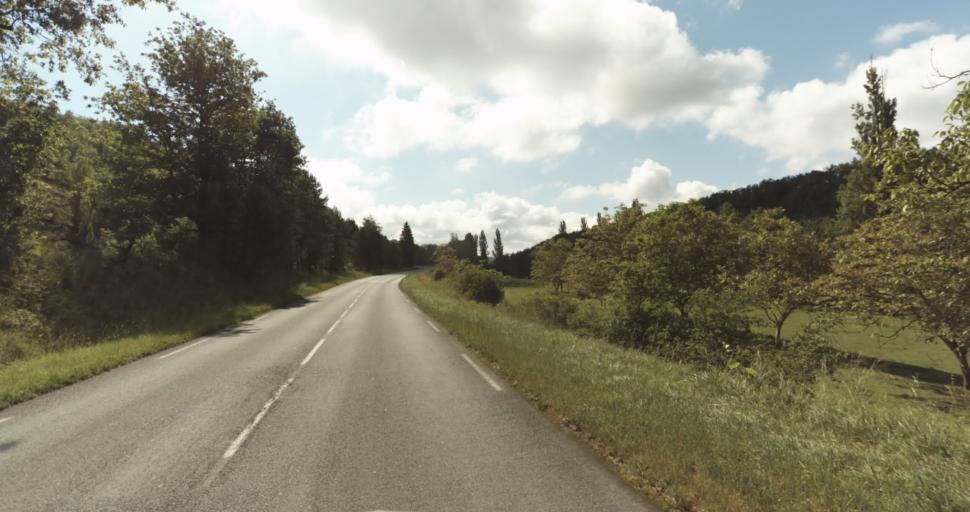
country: FR
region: Aquitaine
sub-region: Departement de la Dordogne
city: Lalinde
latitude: 44.8480
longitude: 0.8171
